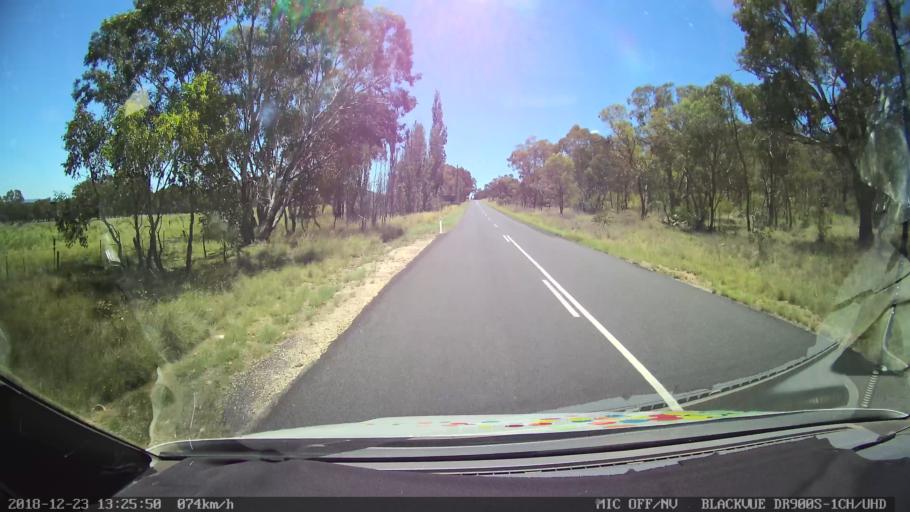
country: AU
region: New South Wales
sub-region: Armidale Dumaresq
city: Armidale
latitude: -30.4739
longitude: 151.3745
